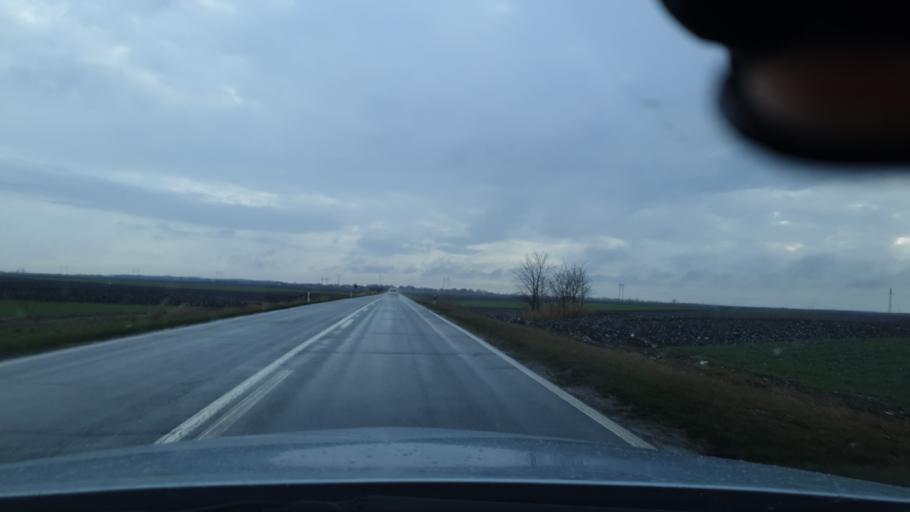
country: RS
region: Autonomna Pokrajina Vojvodina
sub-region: Juznobanatski Okrug
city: Kovin
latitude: 44.8300
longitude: 20.8344
